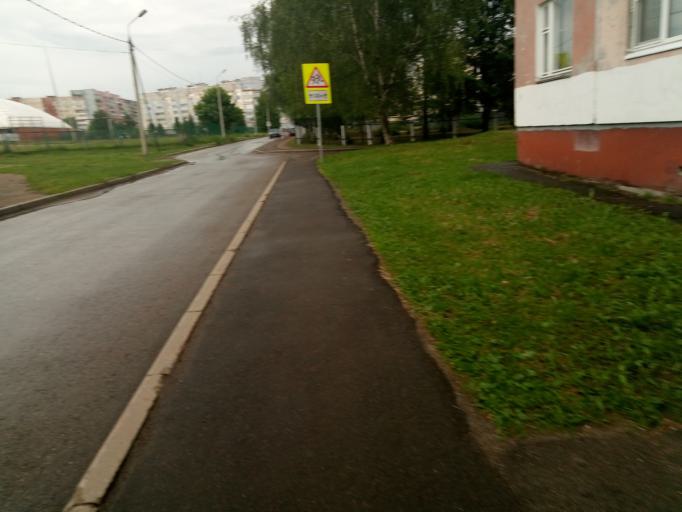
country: RU
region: Jaroslavl
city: Yaroslavl
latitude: 57.6476
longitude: 39.9596
